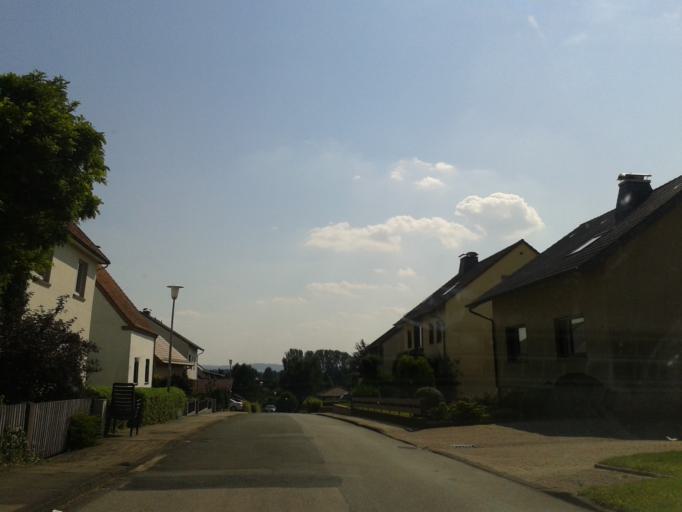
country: DE
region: North Rhine-Westphalia
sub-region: Regierungsbezirk Detmold
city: Steinheim
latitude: 51.8972
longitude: 9.0528
